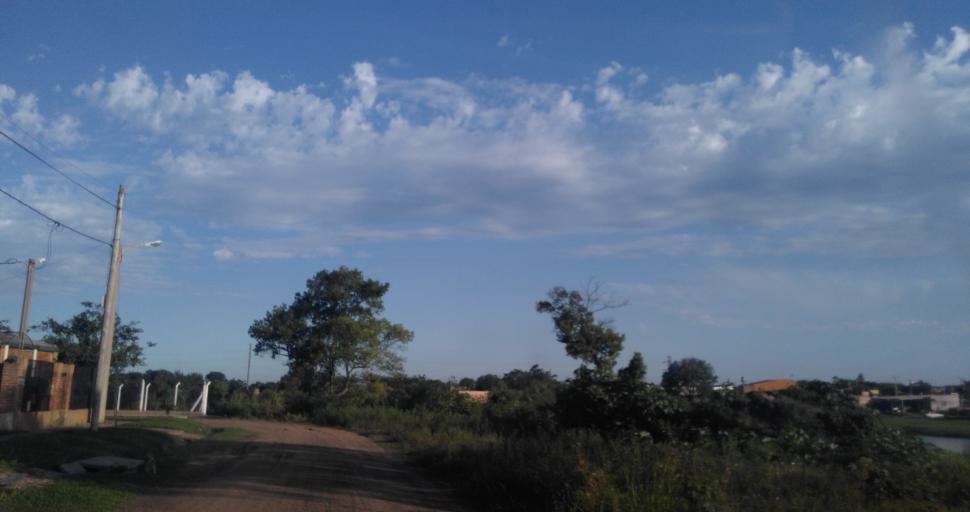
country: AR
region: Chaco
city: Fontana
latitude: -27.4152
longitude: -59.0249
